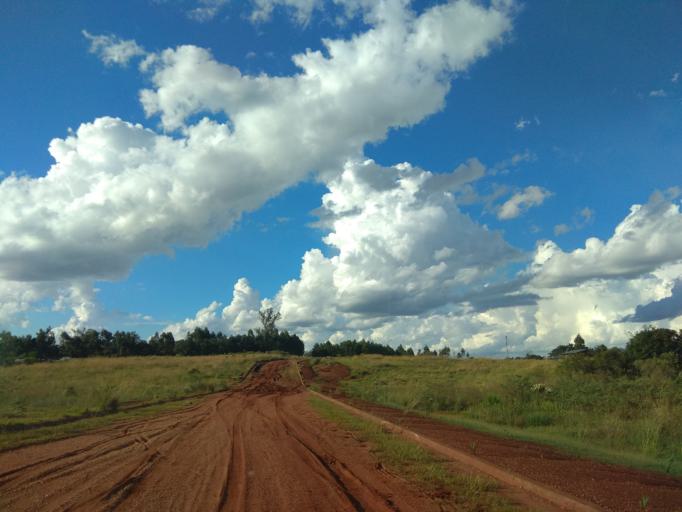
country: AR
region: Misiones
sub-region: Departamento de Candelaria
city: Candelaria
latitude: -27.4836
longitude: -55.7520
